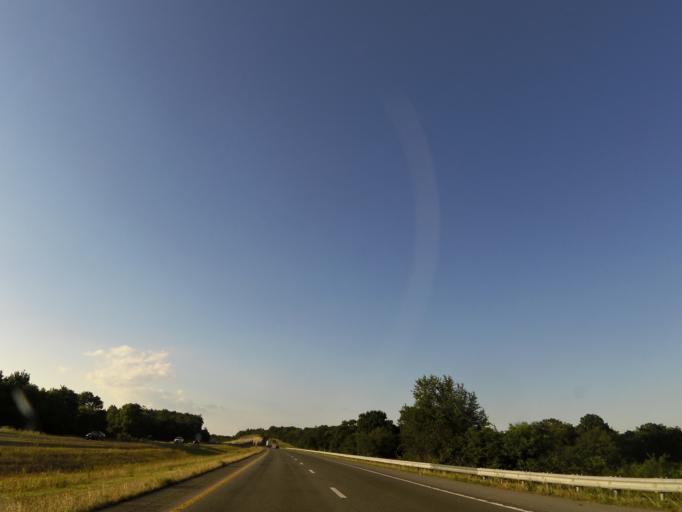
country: US
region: Tennessee
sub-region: Rutherford County
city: Smyrna
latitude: 36.0000
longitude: -86.4296
